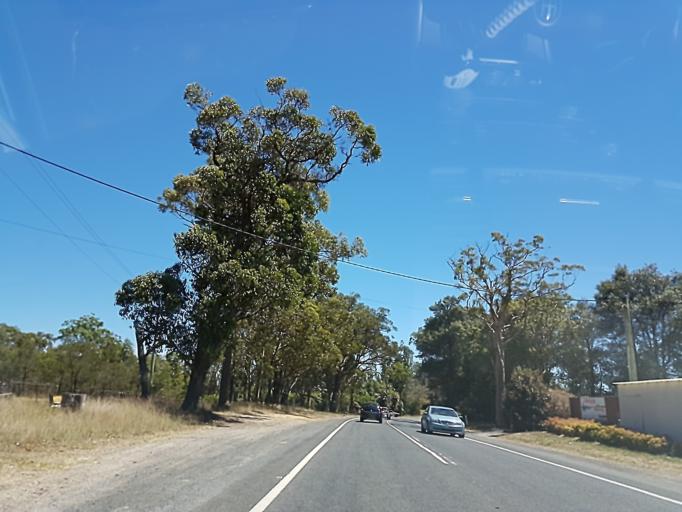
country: AU
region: New South Wales
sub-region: Hornsby Shire
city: Glenorie
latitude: -33.4619
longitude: 150.9948
